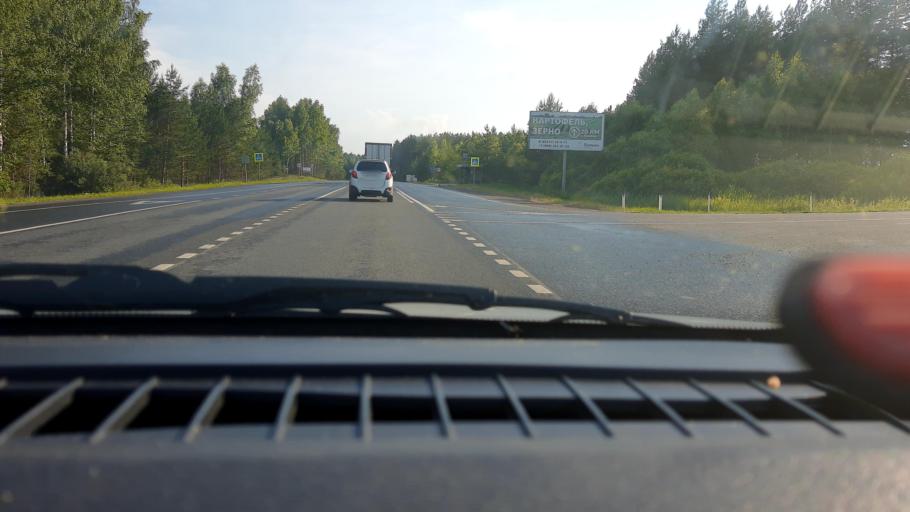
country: RU
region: Nizjnij Novgorod
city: Arzamas
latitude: 55.5157
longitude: 43.9034
